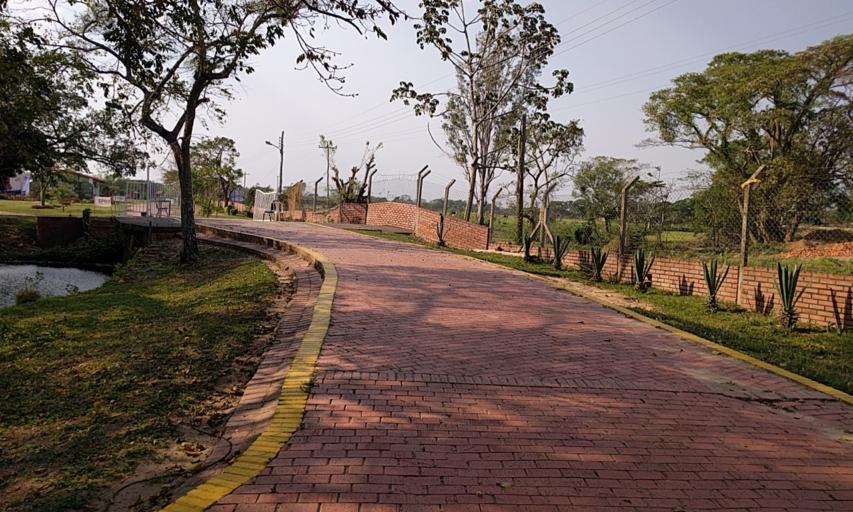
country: BO
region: Santa Cruz
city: Warnes
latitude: -17.4462
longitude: -63.1838
